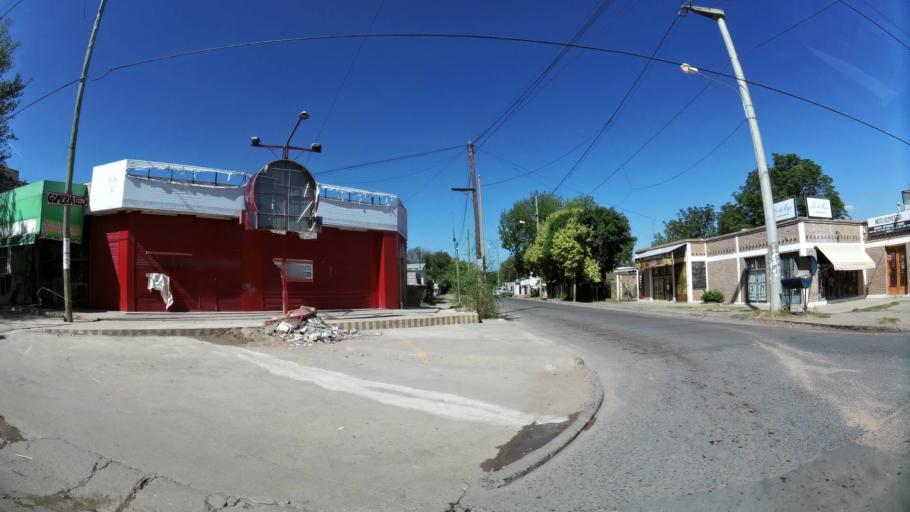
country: AR
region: Cordoba
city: Saldan
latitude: -31.3252
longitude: -64.2886
